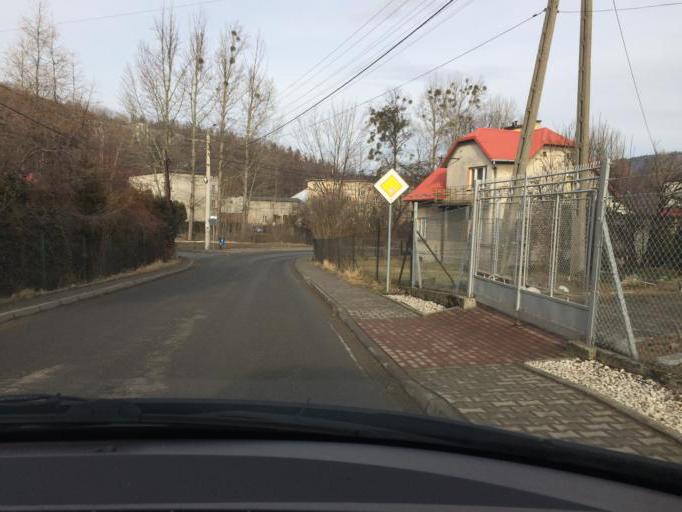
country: PL
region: Silesian Voivodeship
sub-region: Powiat bielski
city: Bystra
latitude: 49.7619
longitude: 19.0660
